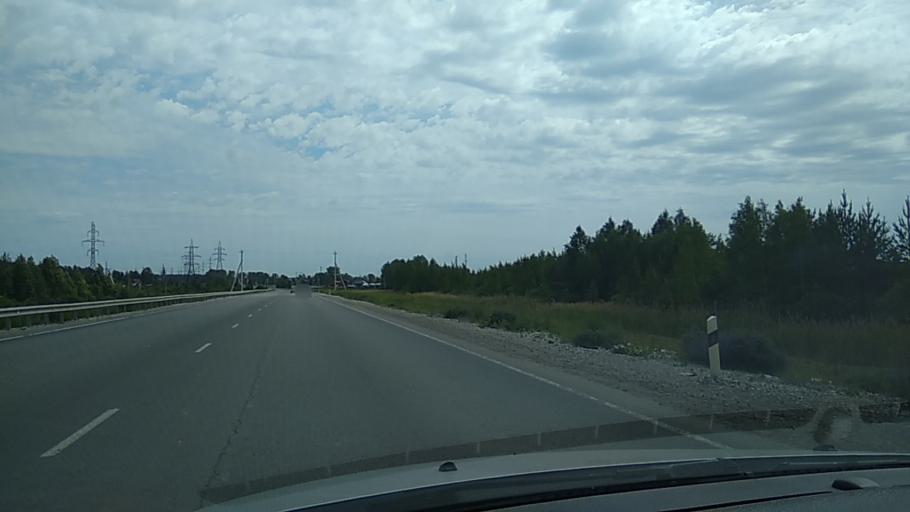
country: RU
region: Sverdlovsk
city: Verkhnyaya Pyshma
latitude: 56.9503
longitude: 60.5914
